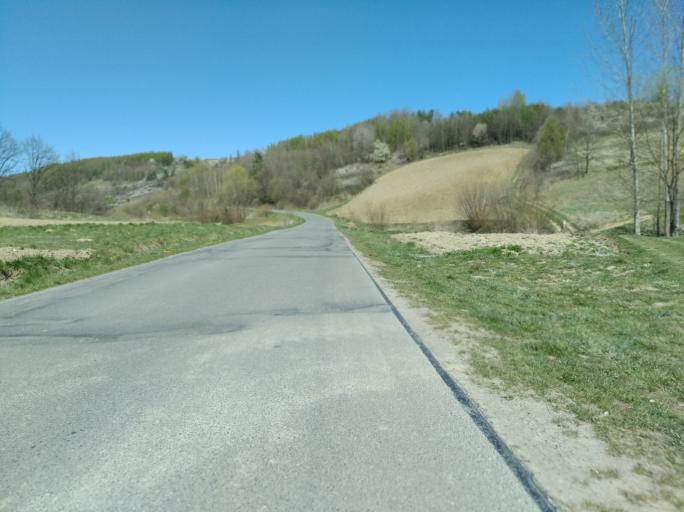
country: PL
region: Subcarpathian Voivodeship
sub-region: Powiat brzozowski
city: Dydnia
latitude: 49.7017
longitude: 22.1525
